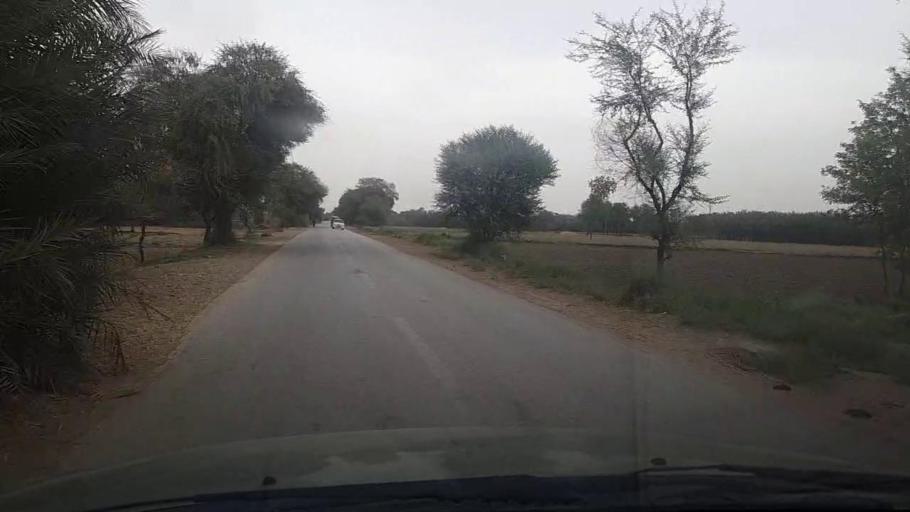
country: PK
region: Sindh
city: Daulatpur
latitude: 26.3266
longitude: 68.1101
